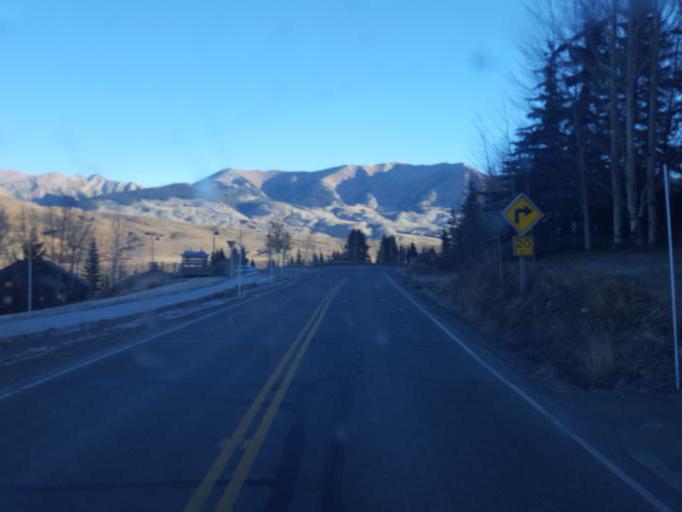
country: US
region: Colorado
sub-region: Gunnison County
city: Crested Butte
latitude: 38.9103
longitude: -106.9673
